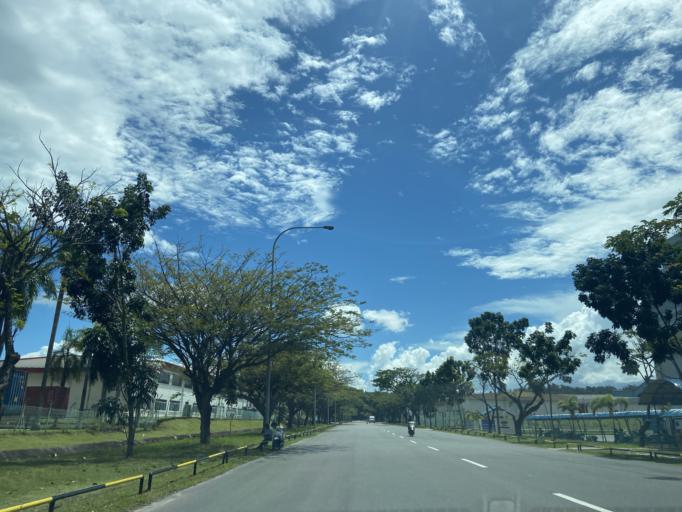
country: SG
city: Singapore
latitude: 1.0601
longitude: 104.0353
